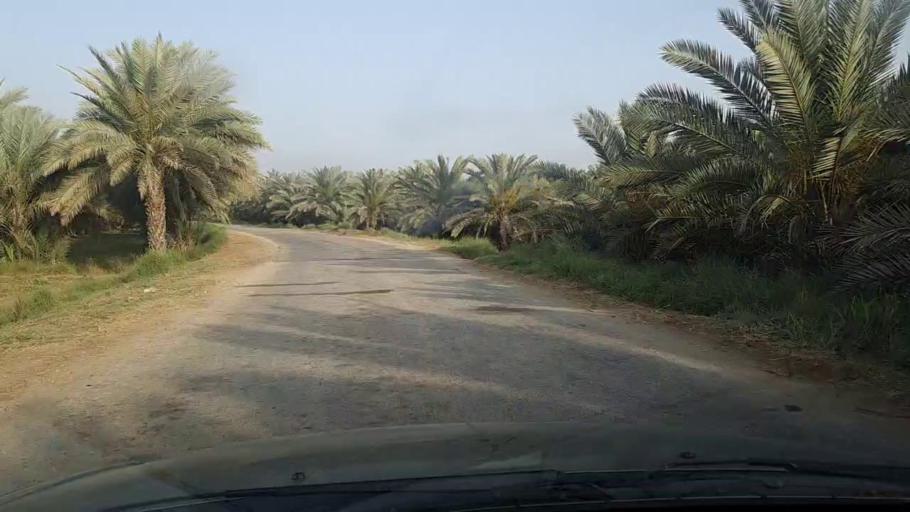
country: PK
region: Sindh
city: Pir jo Goth
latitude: 27.5533
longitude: 68.6865
